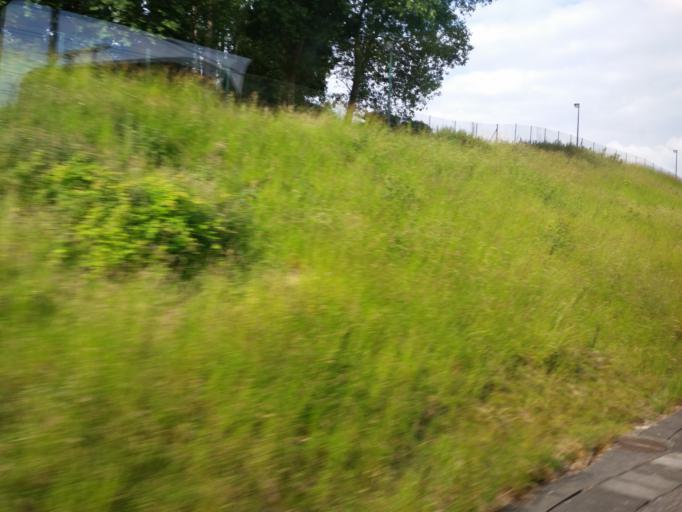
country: BE
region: Flanders
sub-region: Provincie Vlaams-Brabant
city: Diegem
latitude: 50.8919
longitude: 4.4313
